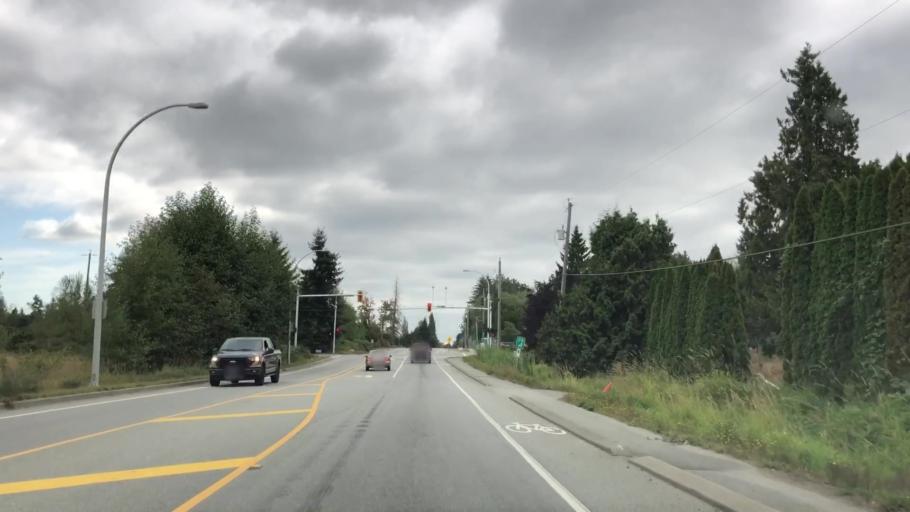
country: CA
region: British Columbia
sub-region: Greater Vancouver Regional District
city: White Rock
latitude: 49.0603
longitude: -122.7583
